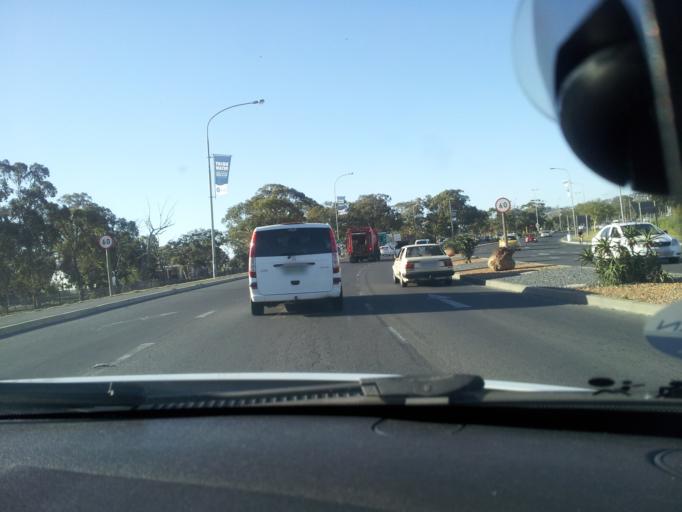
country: ZA
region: Western Cape
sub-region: Cape Winelands District Municipality
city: Stellenbosch
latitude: -34.0918
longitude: 18.8193
